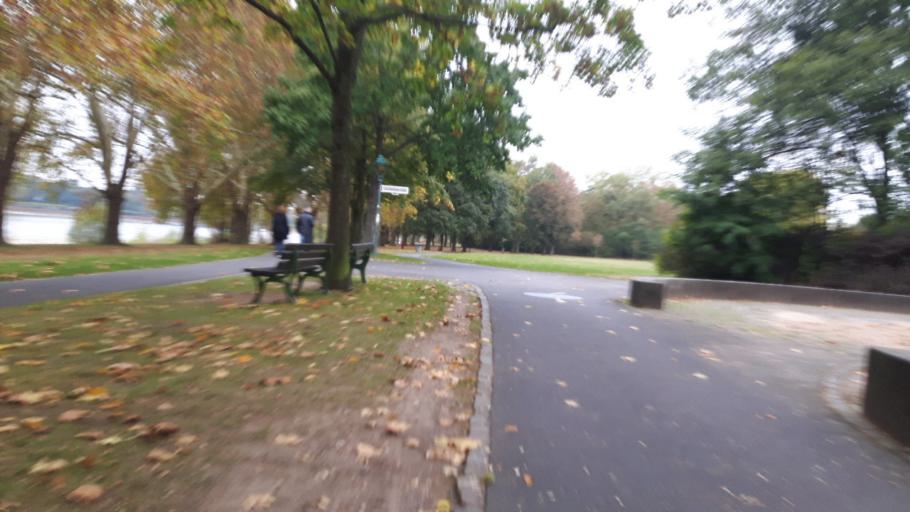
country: DE
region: North Rhine-Westphalia
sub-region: Regierungsbezirk Koln
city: Bonn
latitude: 50.7237
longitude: 7.1304
